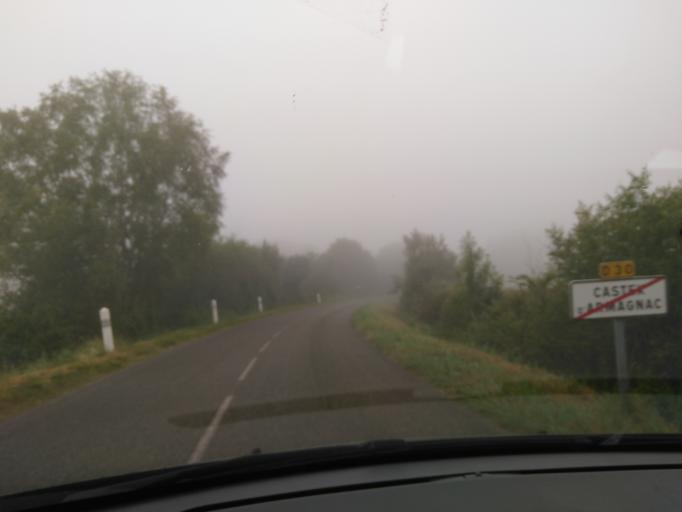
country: FR
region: Midi-Pyrenees
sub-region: Departement du Gers
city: Le Houga
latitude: 43.8591
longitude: -0.1710
